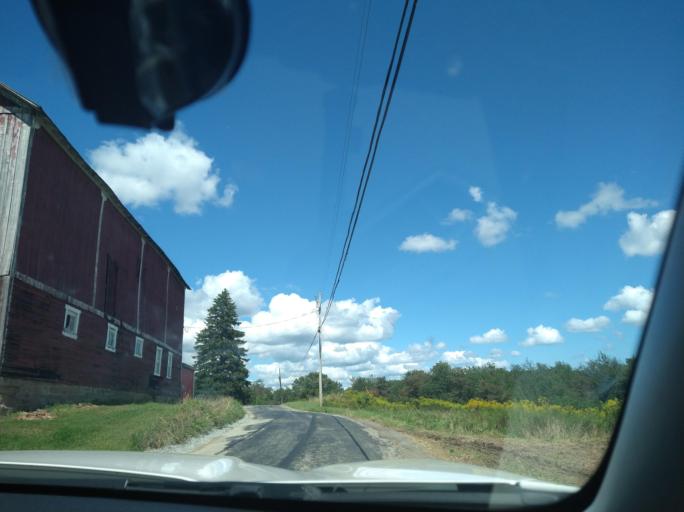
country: US
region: Pennsylvania
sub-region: Fayette County
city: Bear Rocks
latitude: 40.0958
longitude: -79.3647
